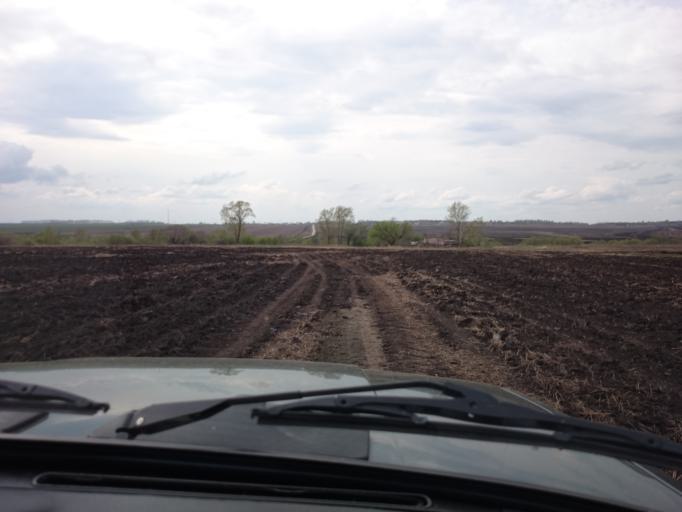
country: RU
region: Mordoviya
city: Kadoshkino
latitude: 54.0178
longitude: 44.4628
